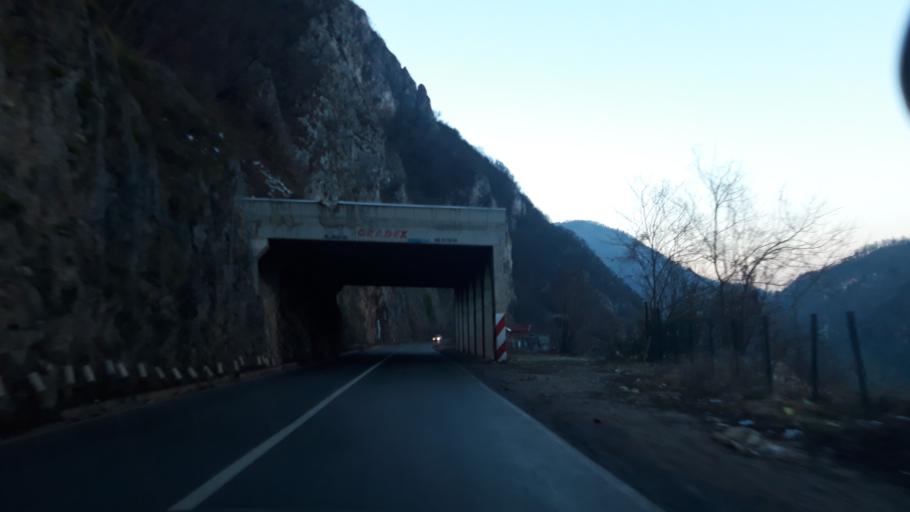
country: RS
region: Central Serbia
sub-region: Macvanski Okrug
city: Mali Zvornik
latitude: 44.3425
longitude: 19.1145
